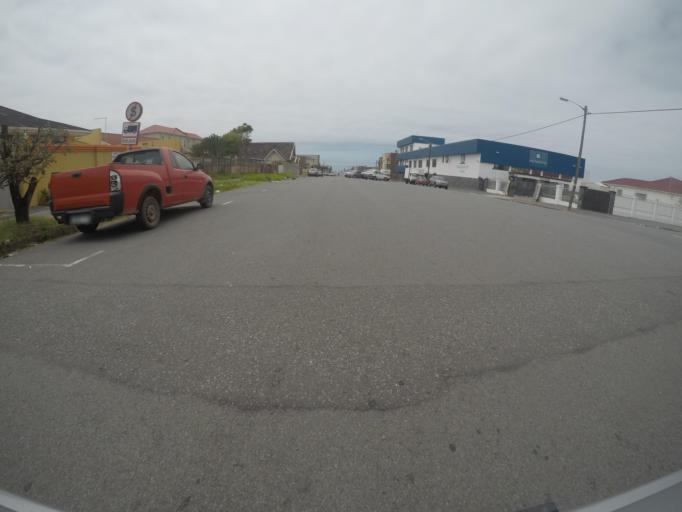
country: ZA
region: Eastern Cape
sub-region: Buffalo City Metropolitan Municipality
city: East London
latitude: -33.0160
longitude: 27.9134
